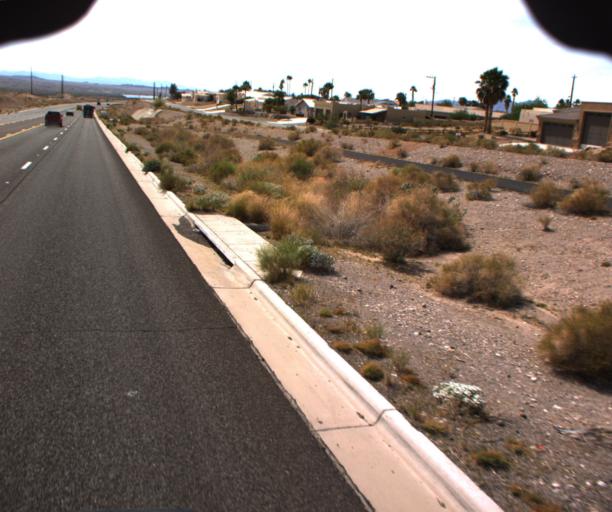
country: US
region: Arizona
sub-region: Mohave County
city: Lake Havasu City
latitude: 34.4533
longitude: -114.3056
